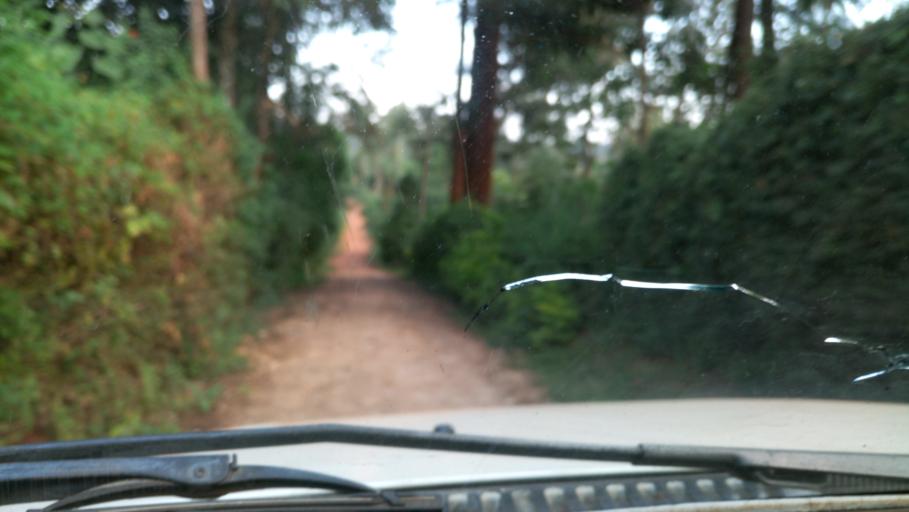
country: KE
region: Murang'a District
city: Kangema
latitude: -0.7127
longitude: 37.0413
